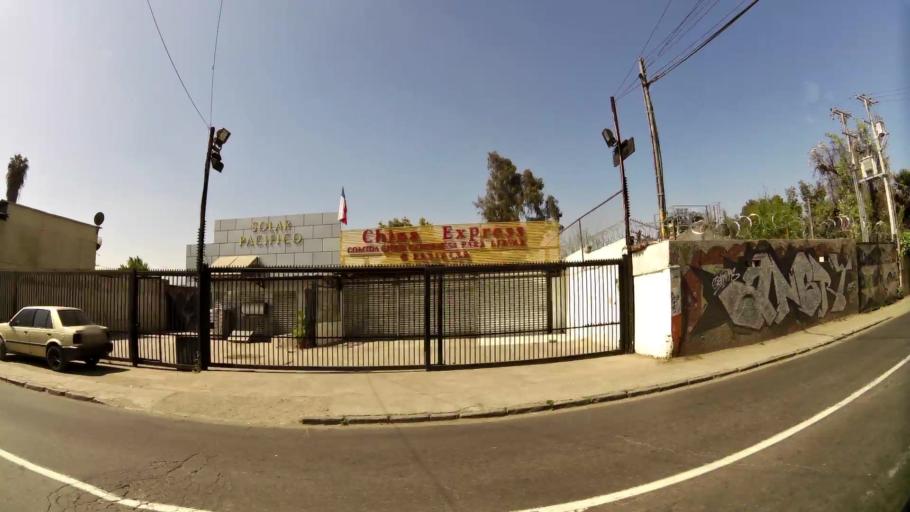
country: CL
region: Santiago Metropolitan
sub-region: Provincia de Santiago
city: Lo Prado
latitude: -33.3695
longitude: -70.7383
